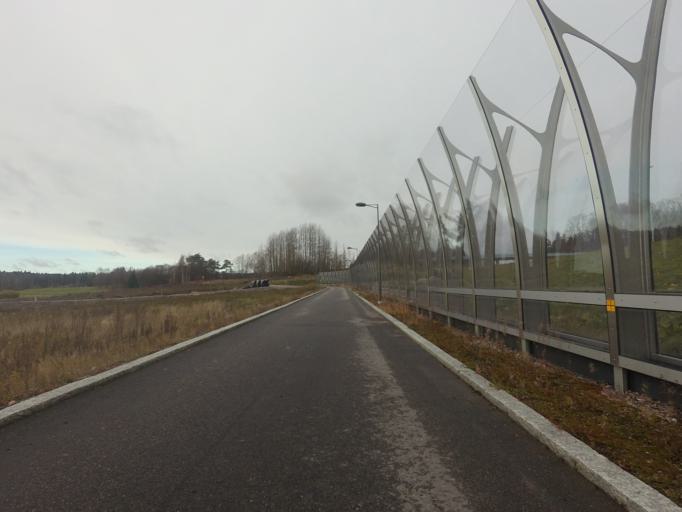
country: FI
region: Uusimaa
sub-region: Helsinki
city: Kauniainen
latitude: 60.1920
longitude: 24.7438
